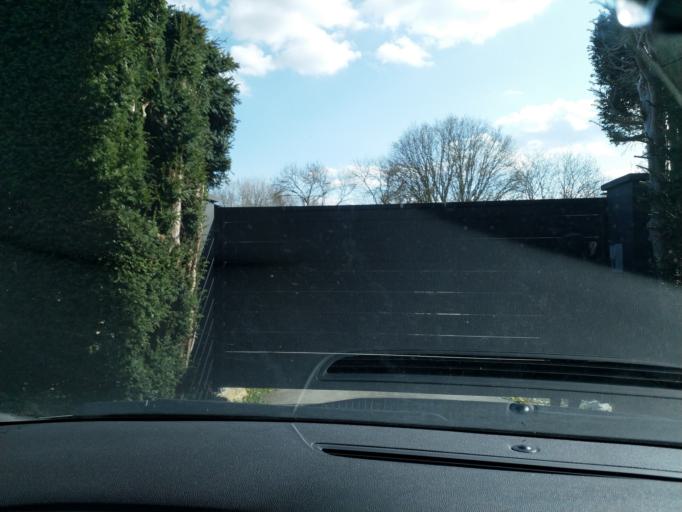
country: GB
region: England
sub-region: Warwickshire
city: Wellesbourne Mountford
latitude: 52.1867
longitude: -1.5552
